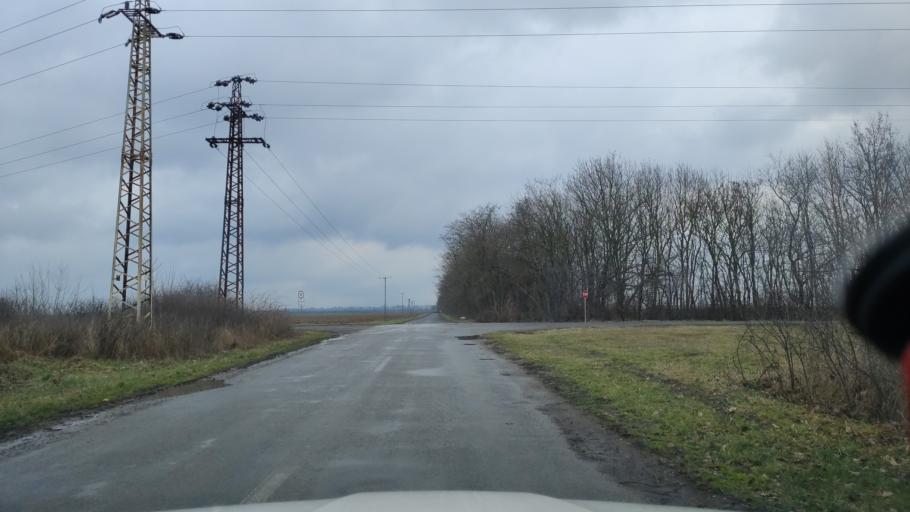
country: HU
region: Hajdu-Bihar
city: Hajduszoboszlo
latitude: 47.4650
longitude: 21.4144
